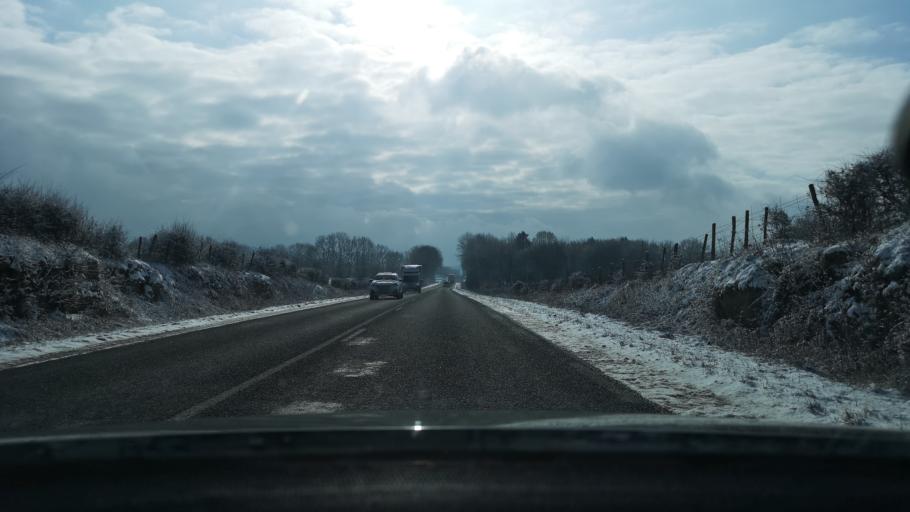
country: FR
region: Franche-Comte
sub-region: Departement du Jura
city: Orgelet
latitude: 46.5654
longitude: 5.5948
